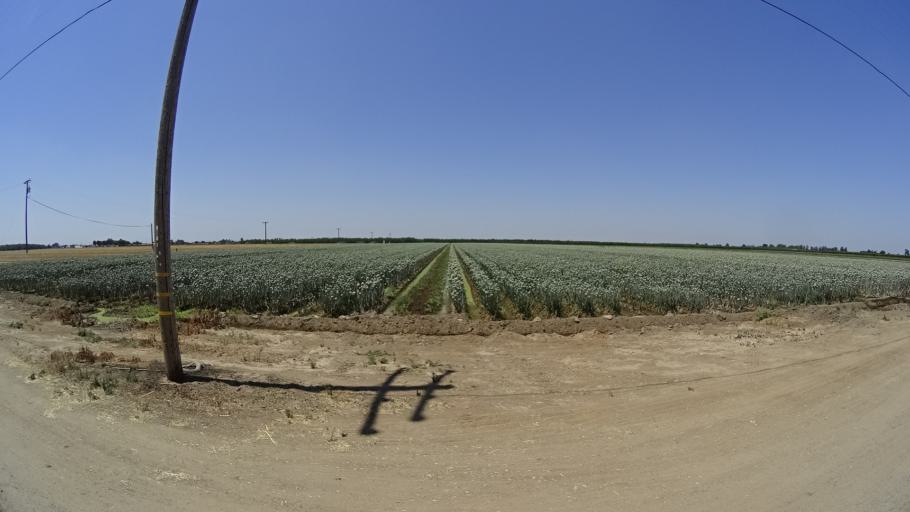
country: US
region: California
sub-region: Kings County
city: Armona
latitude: 36.3490
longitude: -119.7270
